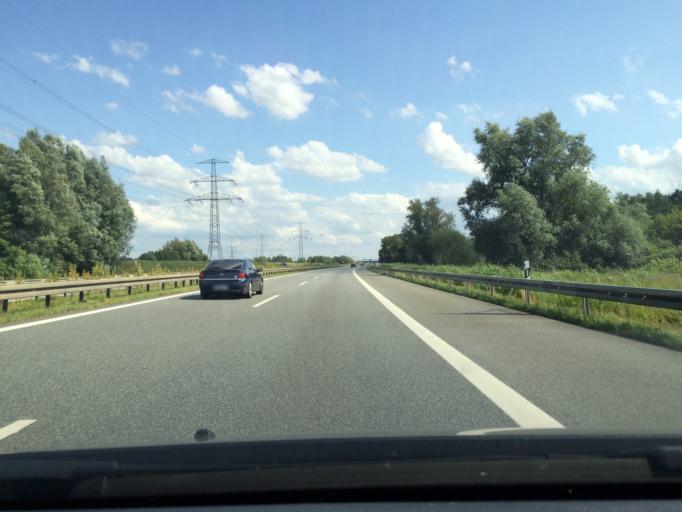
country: DE
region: Mecklenburg-Vorpommern
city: Dierkow-West
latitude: 54.1254
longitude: 12.1550
